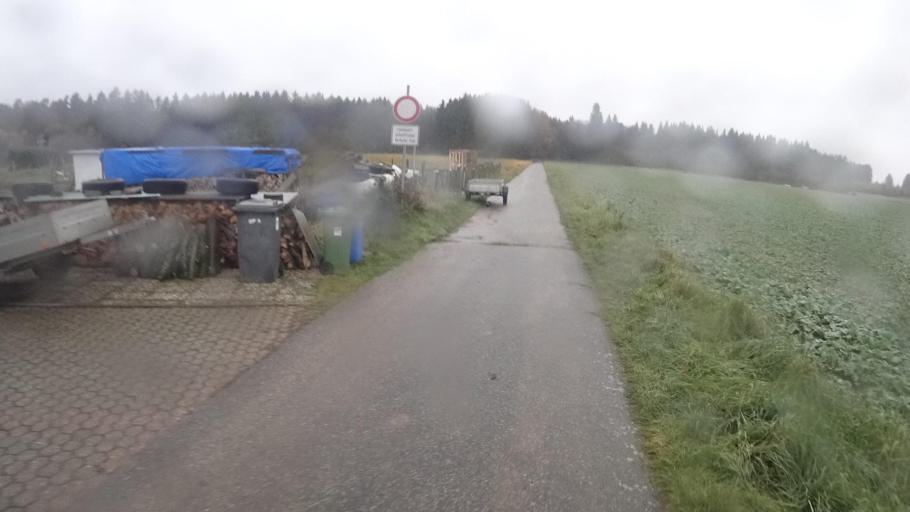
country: DE
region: Rheinland-Pfalz
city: Maisborn
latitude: 50.0831
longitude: 7.5824
